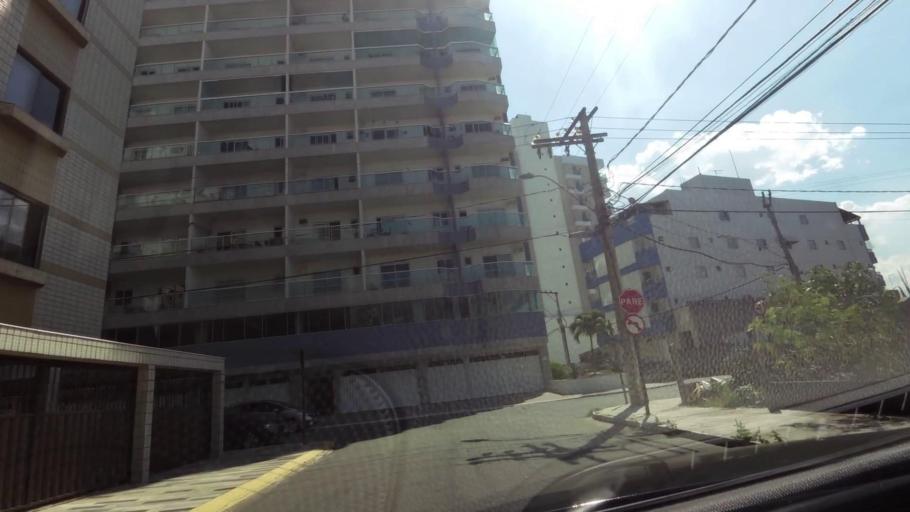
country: BR
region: Espirito Santo
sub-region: Guarapari
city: Guarapari
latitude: -20.6521
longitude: -40.4758
